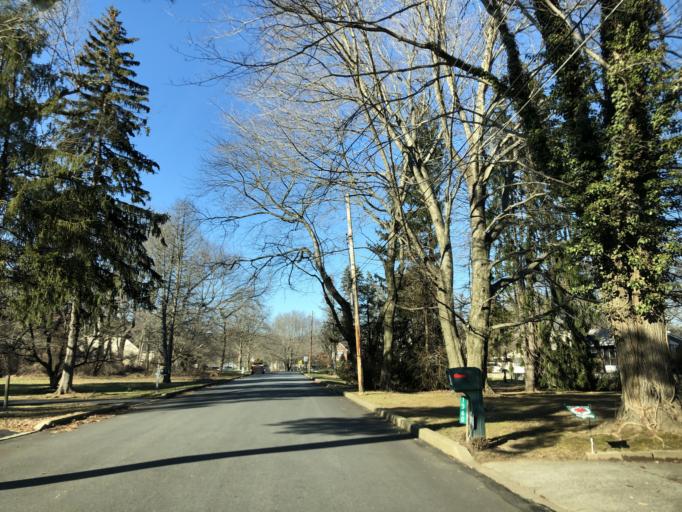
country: US
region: Pennsylvania
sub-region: Delaware County
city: Chester Heights
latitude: 39.8564
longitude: -75.4677
